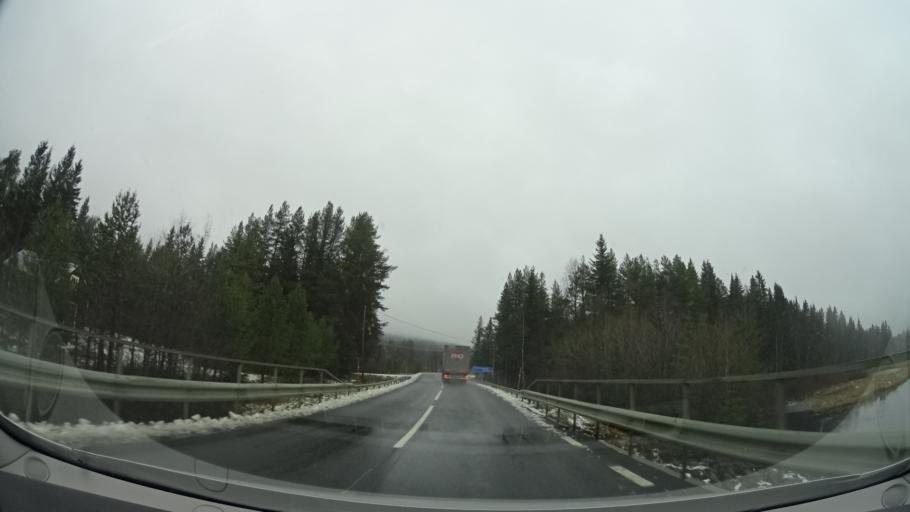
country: SE
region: Vaesterbotten
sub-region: Dorotea Kommun
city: Dorotea
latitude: 64.2561
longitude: 16.3705
